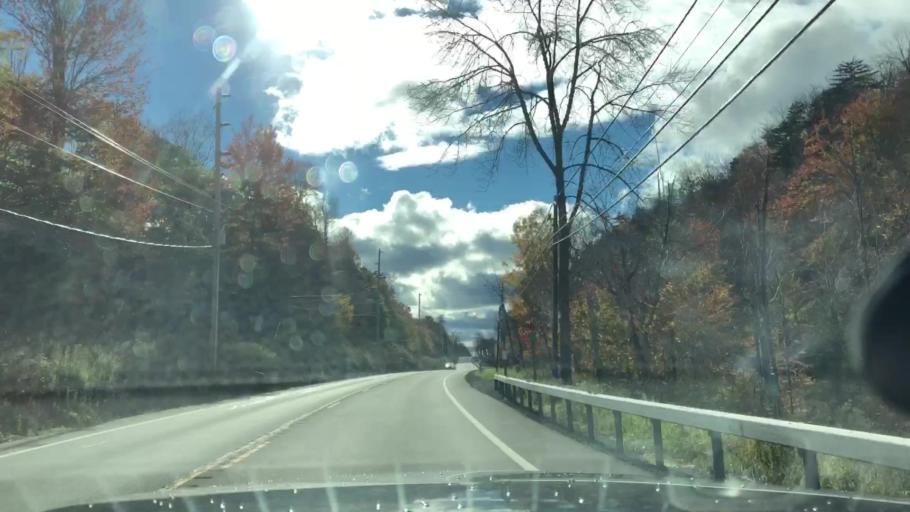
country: US
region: New York
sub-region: Oneida County
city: Boonville
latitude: 43.7265
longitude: -74.9327
